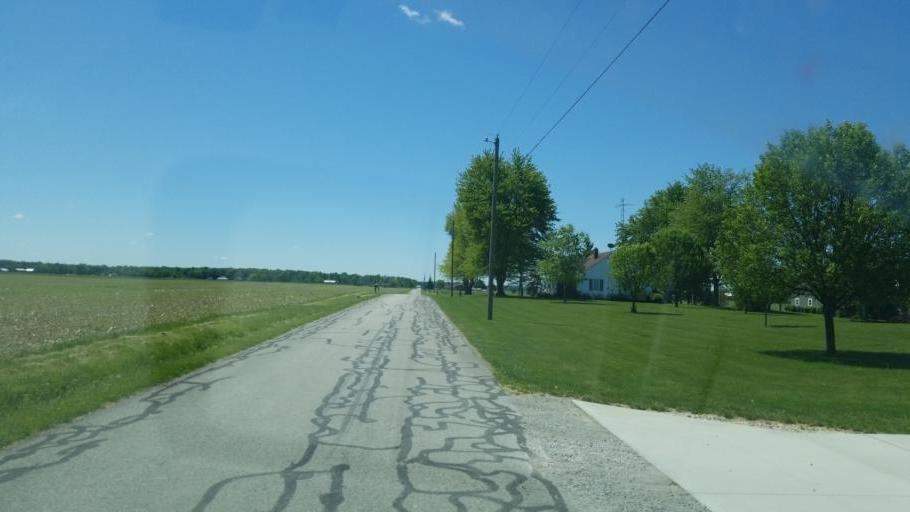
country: US
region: Ohio
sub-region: Shelby County
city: Fort Loramie
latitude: 40.3691
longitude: -84.3166
